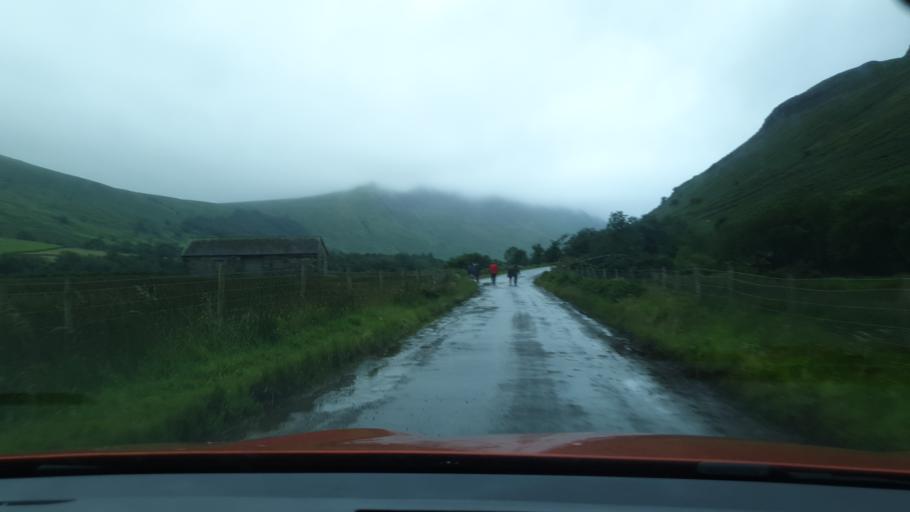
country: GB
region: England
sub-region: Cumbria
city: Keswick
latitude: 54.4634
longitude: -3.2593
